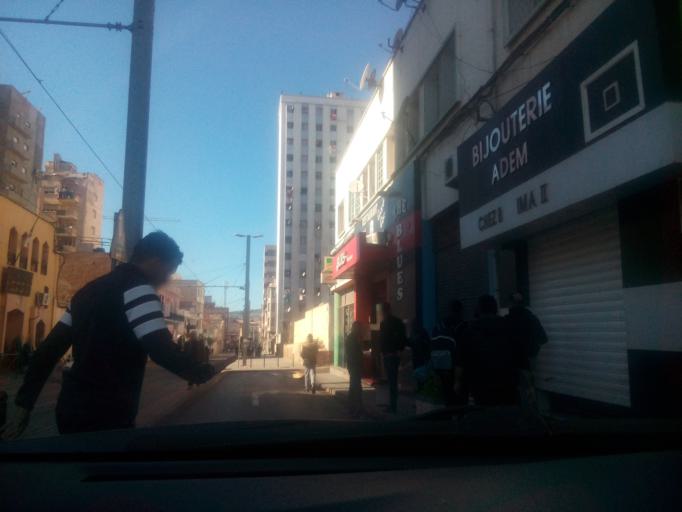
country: DZ
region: Oran
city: Oran
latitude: 35.6988
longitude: -0.6308
